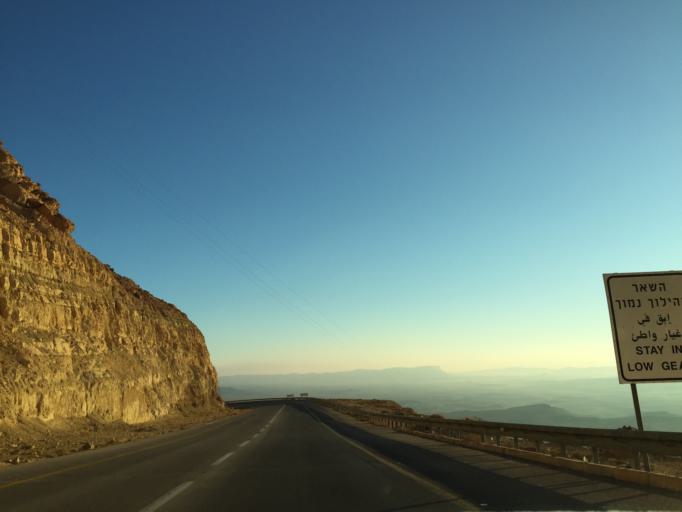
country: IL
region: Southern District
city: Mitzpe Ramon
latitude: 30.6189
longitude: 34.8131
